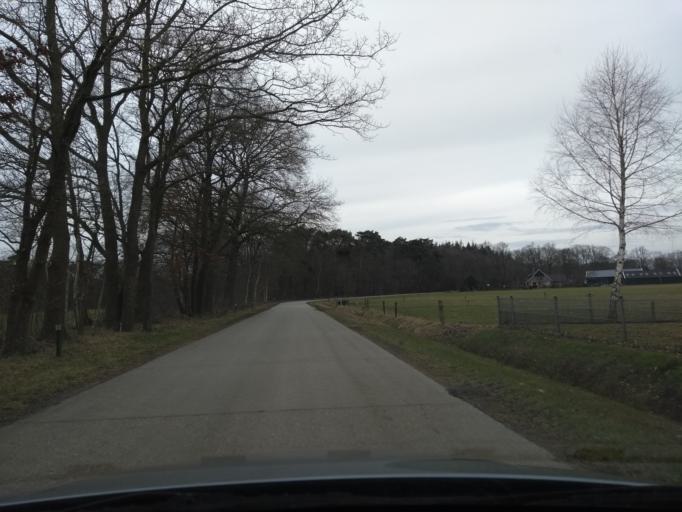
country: NL
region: Overijssel
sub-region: Gemeente Almelo
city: Almelo
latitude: 52.3616
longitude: 6.7194
